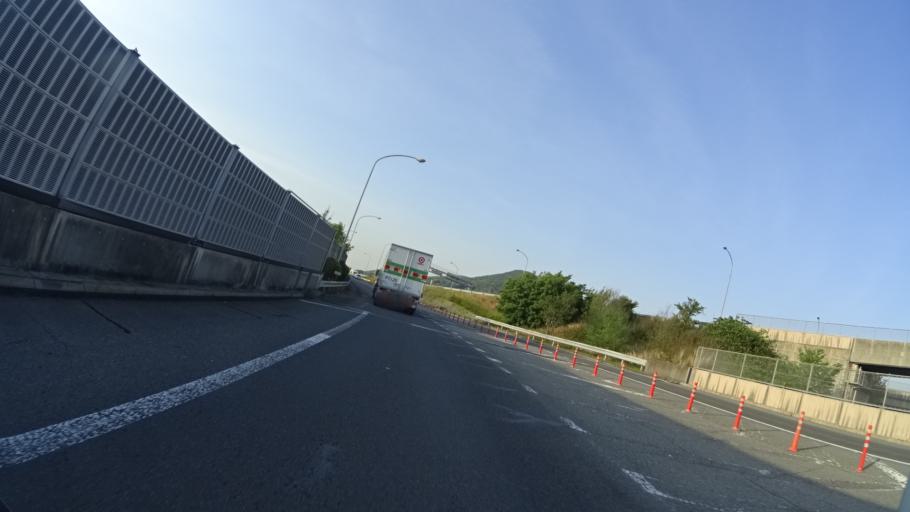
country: JP
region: Kagawa
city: Sakaidecho
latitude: 34.2829
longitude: 133.8512
